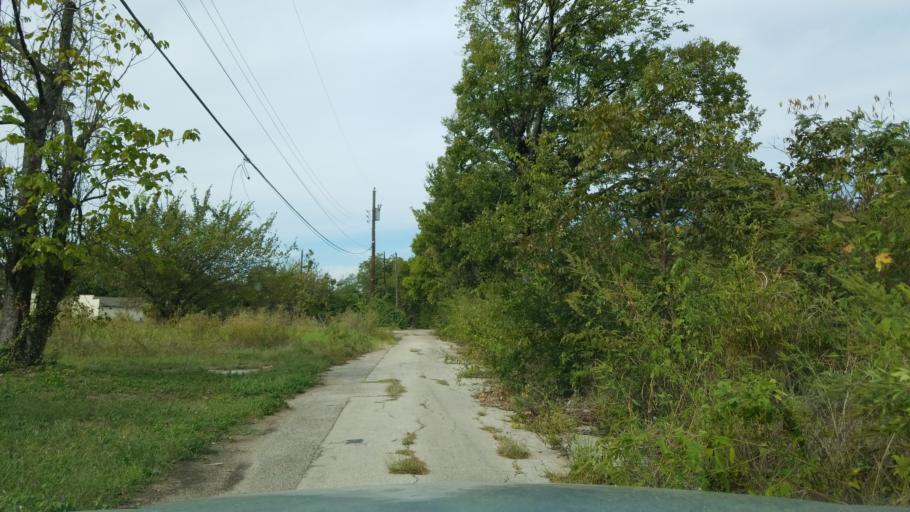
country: US
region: Texas
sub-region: Dallas County
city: Dallas
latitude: 32.7784
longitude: -96.7392
